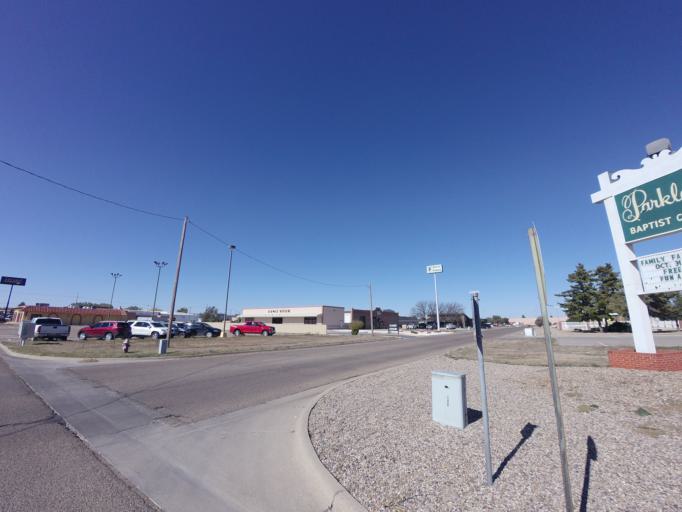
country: US
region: New Mexico
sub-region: Curry County
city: Clovis
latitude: 34.4216
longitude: -103.1945
